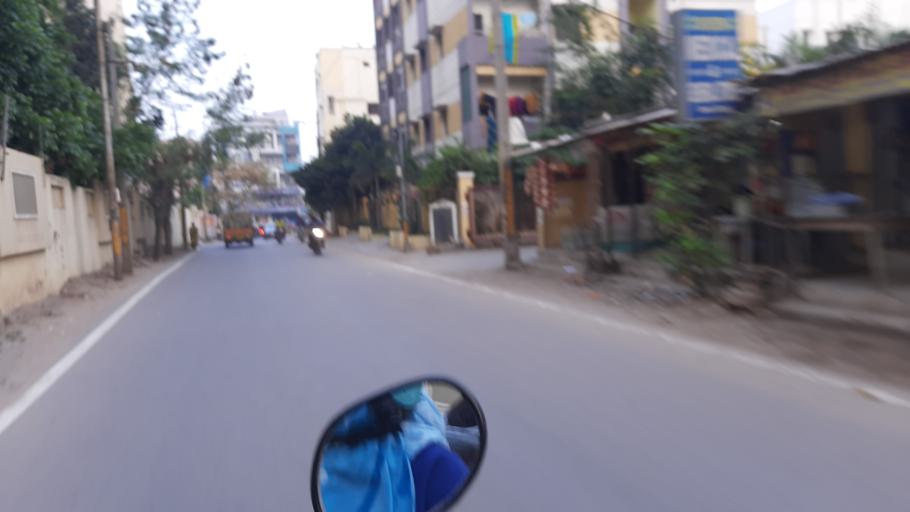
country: IN
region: Telangana
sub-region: Rangareddi
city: Kukatpalli
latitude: 17.4963
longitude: 78.4190
